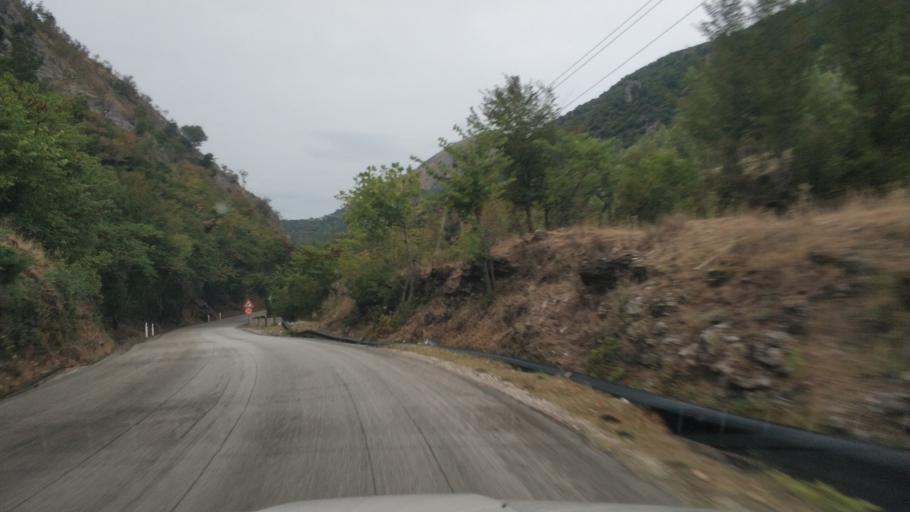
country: AL
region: Vlore
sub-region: Rrethi i Delvines
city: Mesopotam
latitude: 39.9191
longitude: 20.1456
